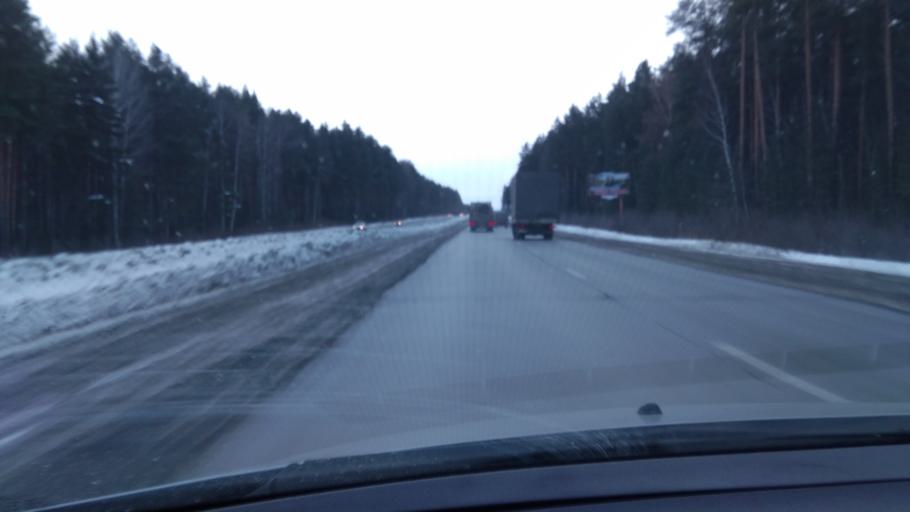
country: RU
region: Sverdlovsk
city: Sysert'
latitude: 56.5735
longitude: 60.8596
